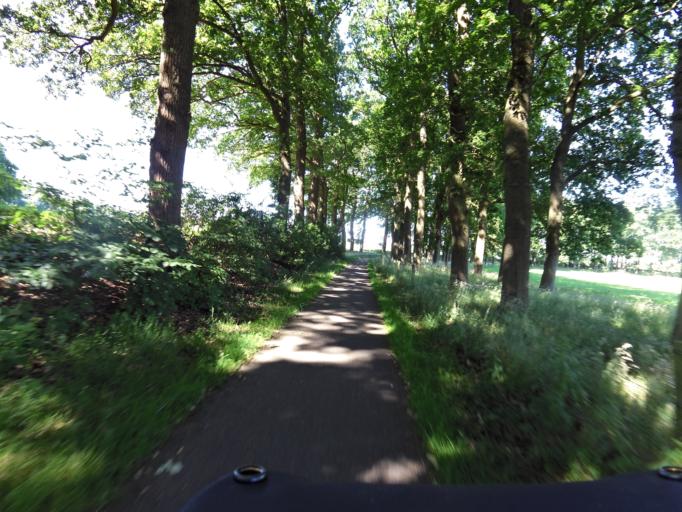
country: NL
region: Overijssel
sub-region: Gemeente Dalfsen
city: Dalfsen
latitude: 52.5123
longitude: 6.3460
